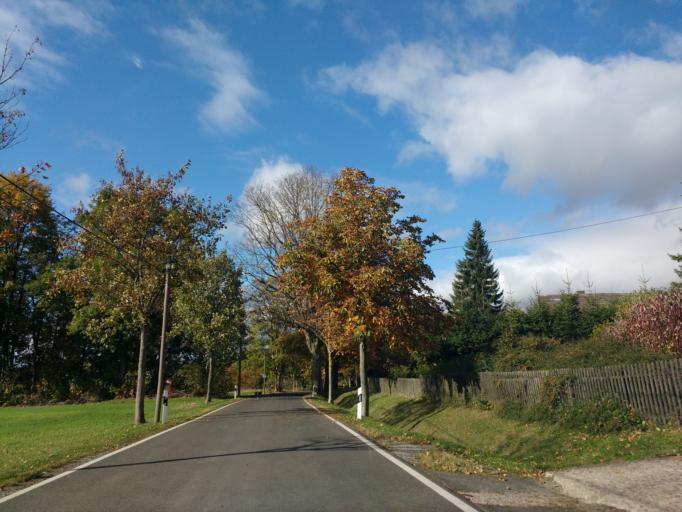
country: DE
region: Thuringia
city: Worbis
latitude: 51.4522
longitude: 10.3489
